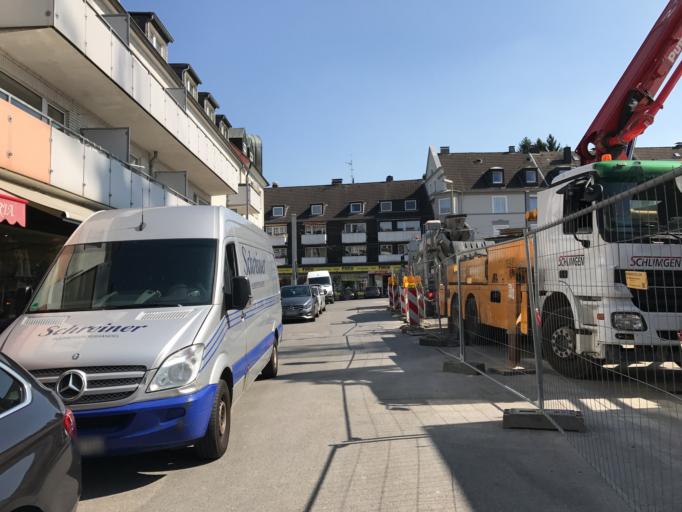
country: DE
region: North Rhine-Westphalia
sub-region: Regierungsbezirk Dusseldorf
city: Essen
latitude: 51.4124
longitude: 6.9932
